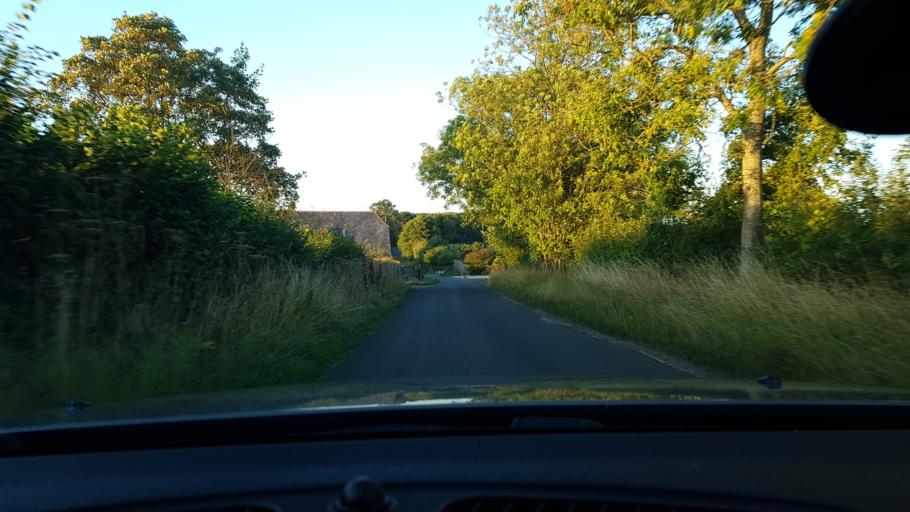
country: GB
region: England
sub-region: West Berkshire
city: Hungerford
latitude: 51.3947
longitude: -1.5223
